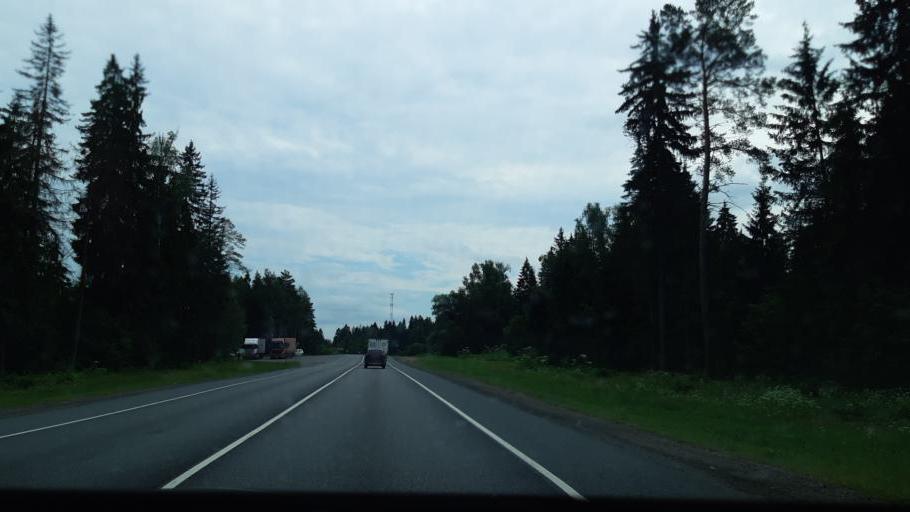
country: RU
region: Moskovskaya
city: Dorokhovo
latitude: 55.4833
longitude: 36.3569
